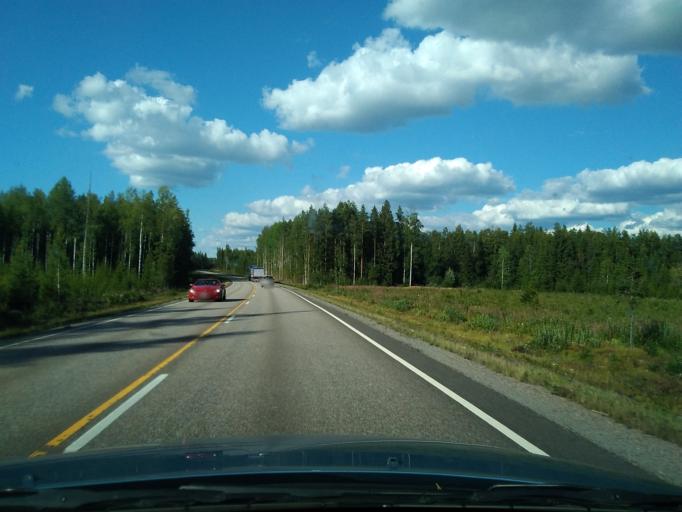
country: FI
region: Pirkanmaa
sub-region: Ylae-Pirkanmaa
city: Maenttae
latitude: 62.1050
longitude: 24.7377
